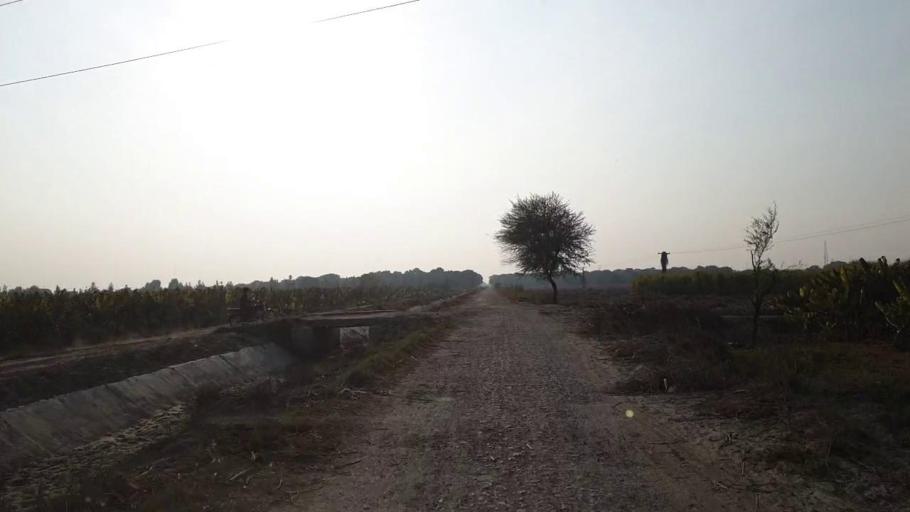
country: PK
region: Sindh
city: Matiari
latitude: 25.5896
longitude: 68.4630
